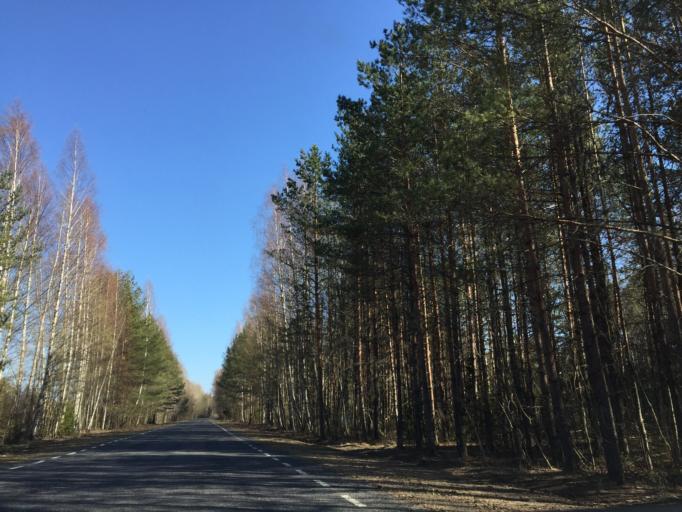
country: EE
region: Ida-Virumaa
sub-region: Johvi vald
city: Johvi
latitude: 59.0163
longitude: 27.4242
